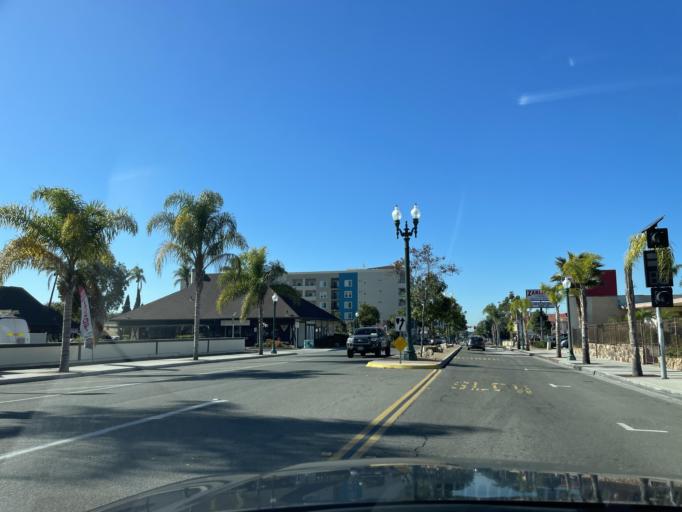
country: US
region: California
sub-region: San Diego County
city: National City
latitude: 32.6776
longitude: -117.1009
